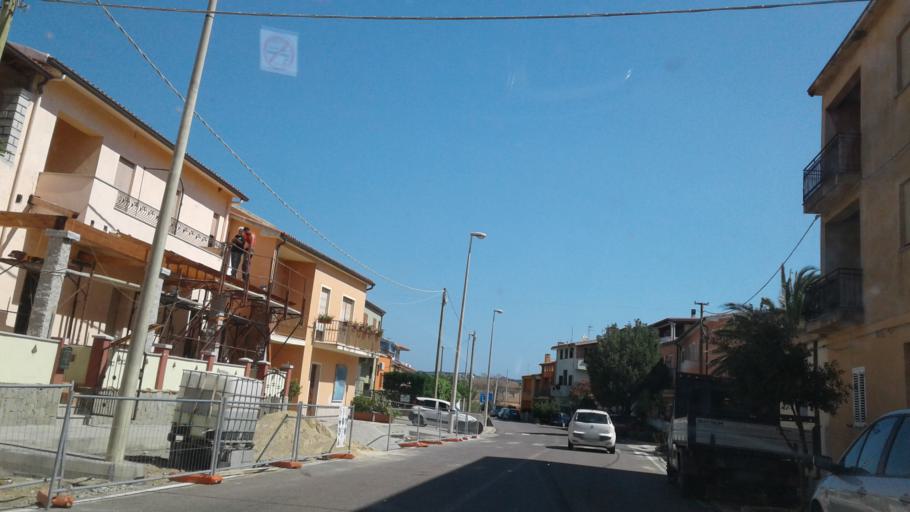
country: IT
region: Sardinia
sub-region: Provincia di Olbia-Tempio
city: Luogosanto
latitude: 41.1094
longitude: 9.2618
